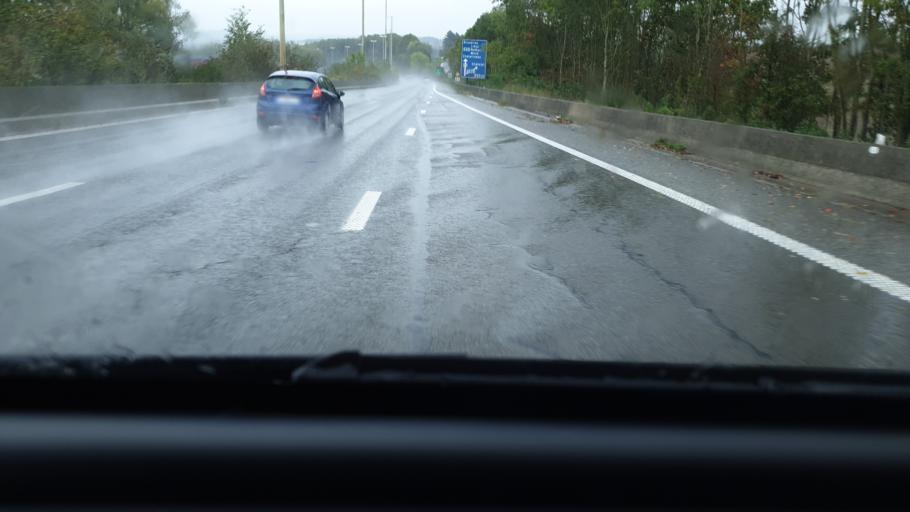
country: BE
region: Wallonia
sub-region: Province du Hainaut
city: Chatelet
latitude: 50.3866
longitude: 4.4955
